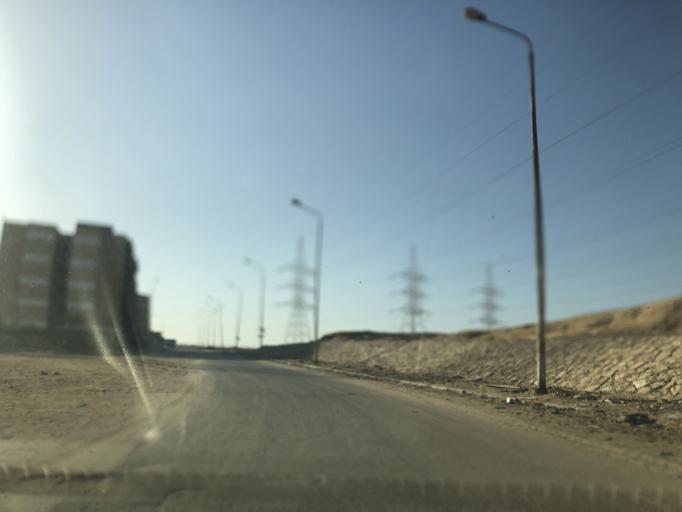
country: EG
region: Al Jizah
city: Al Jizah
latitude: 29.9876
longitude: 31.1093
